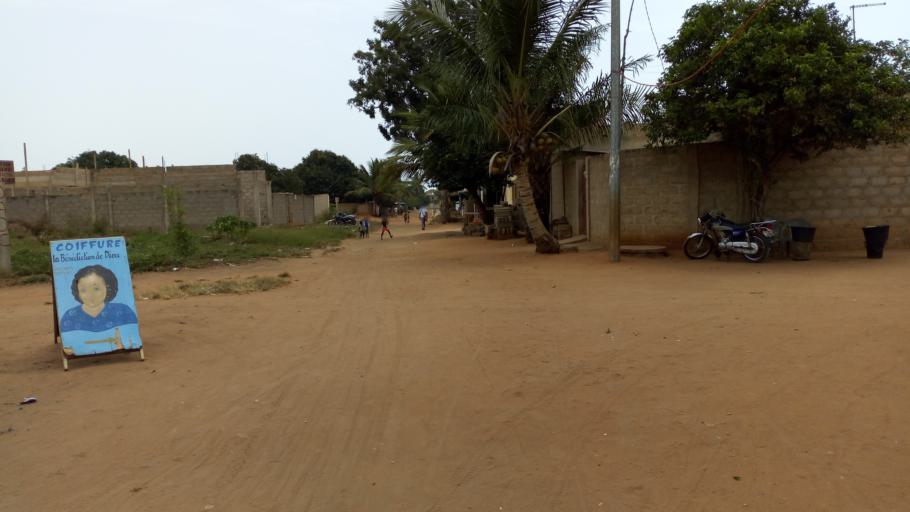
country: TG
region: Maritime
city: Lome
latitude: 6.2233
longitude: 1.1662
